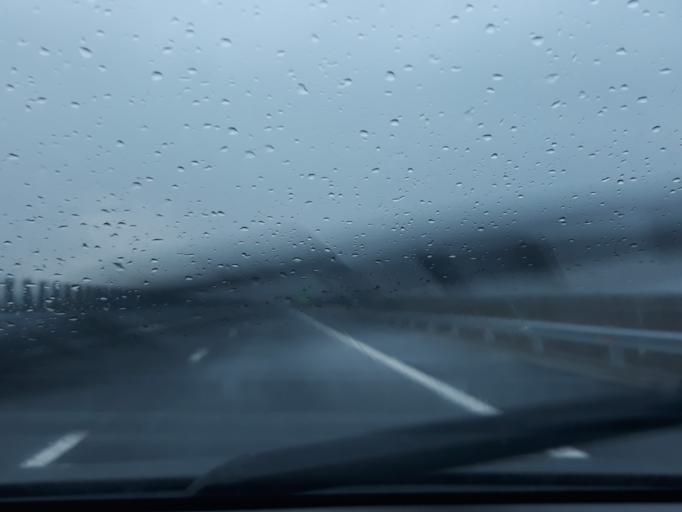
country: RO
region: Mures
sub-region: Comuna Ogra
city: Ogra
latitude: 46.4366
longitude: 24.3138
